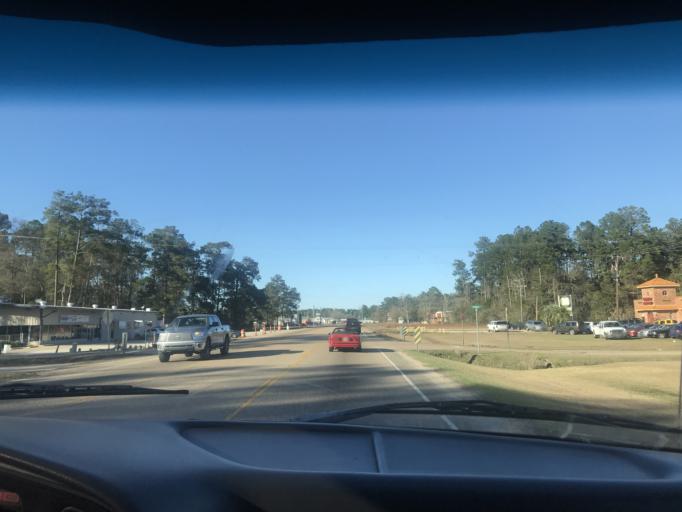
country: US
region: Louisiana
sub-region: Saint Tammany Parish
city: Covington
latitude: 30.4871
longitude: -90.0943
